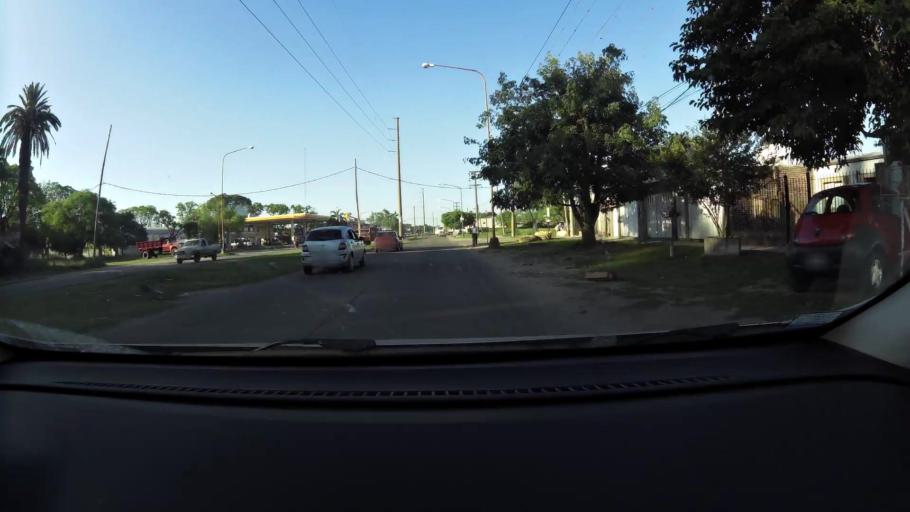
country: AR
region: Santa Fe
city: Santa Fe de la Vera Cruz
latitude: -31.5856
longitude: -60.6907
